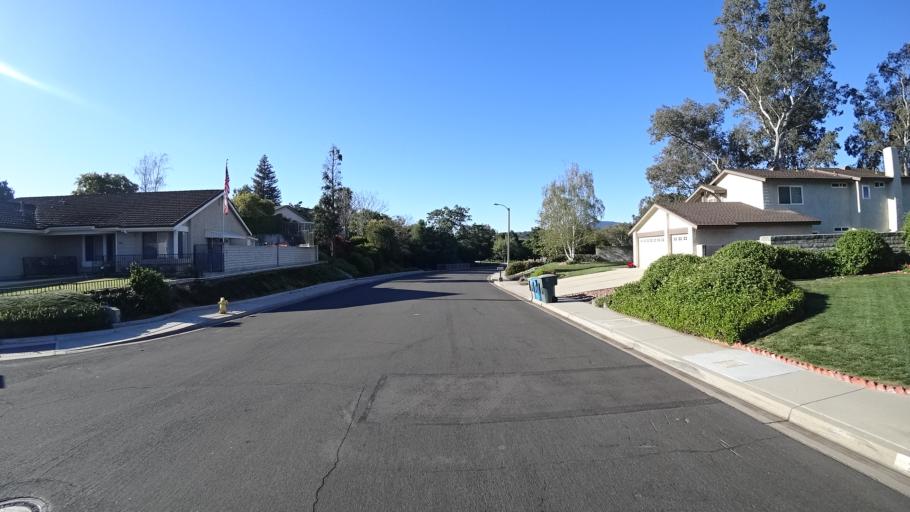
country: US
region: California
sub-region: Ventura County
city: Casa Conejo
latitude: 34.2180
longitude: -118.8913
